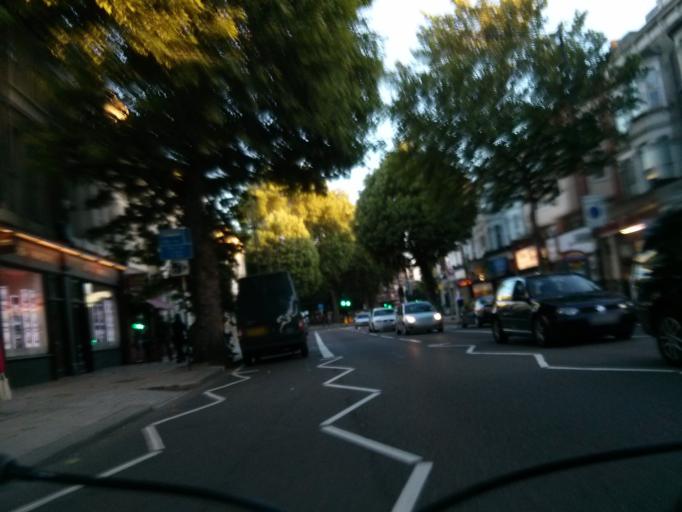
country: GB
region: England
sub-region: Greater London
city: Hammersmith
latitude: 51.4981
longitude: -0.2224
